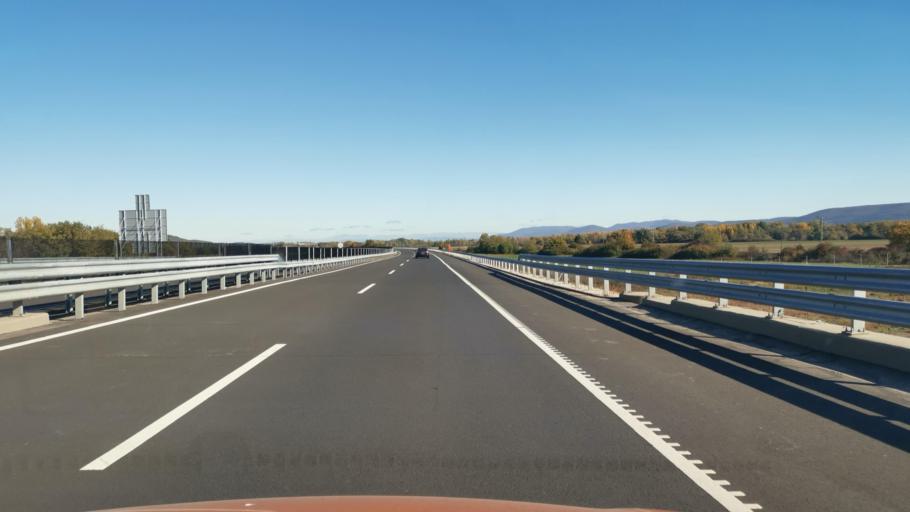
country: HU
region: Borsod-Abauj-Zemplen
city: Gonc
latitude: 48.4293
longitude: 21.1835
